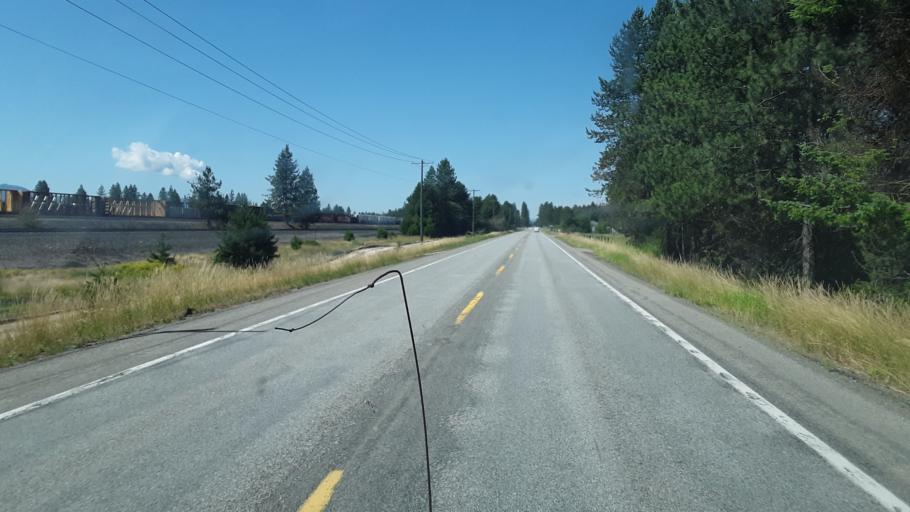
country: US
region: Idaho
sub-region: Kootenai County
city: Post Falls
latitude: 47.7807
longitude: -116.9514
